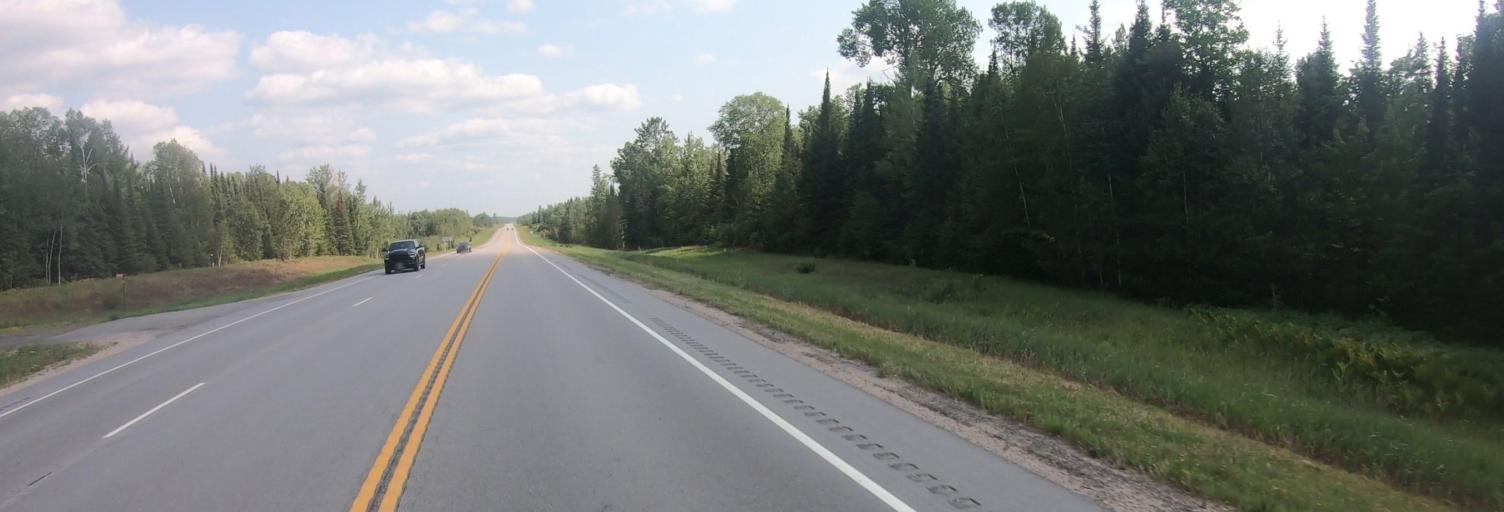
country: US
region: Minnesota
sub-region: Saint Louis County
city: Mountain Iron
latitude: 47.9123
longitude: -92.8048
